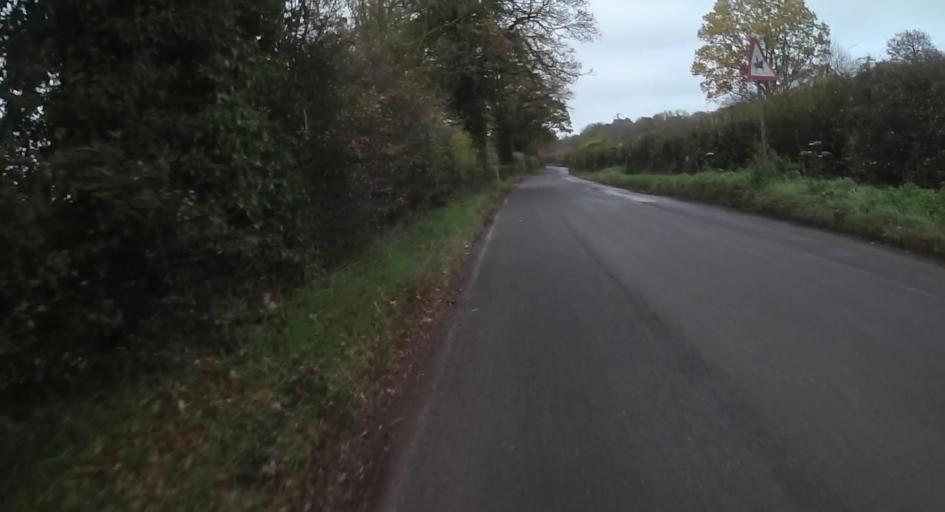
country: GB
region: England
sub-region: Wokingham
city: Swallowfield
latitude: 51.3790
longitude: -0.9350
